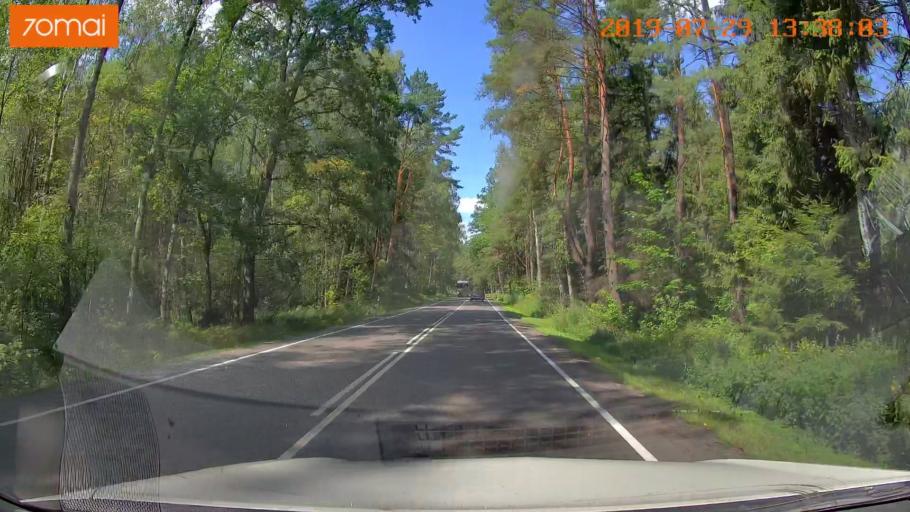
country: RU
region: Kaliningrad
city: Volochayevskoye
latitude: 54.7184
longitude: 20.1759
